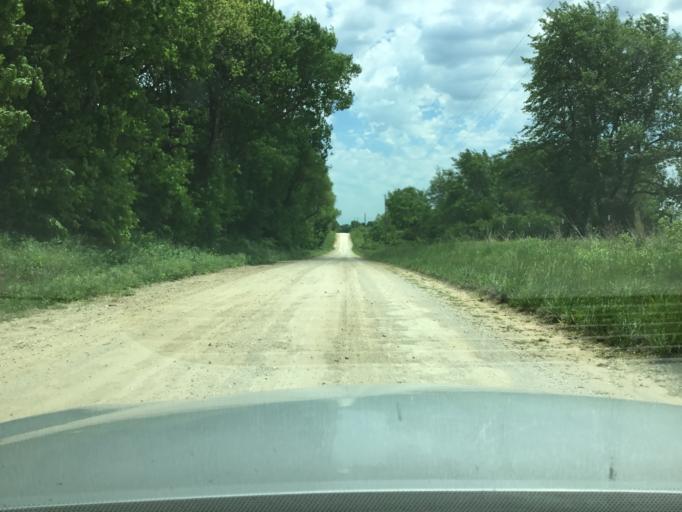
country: US
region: Kansas
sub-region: Montgomery County
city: Caney
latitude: 37.0953
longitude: -95.8166
